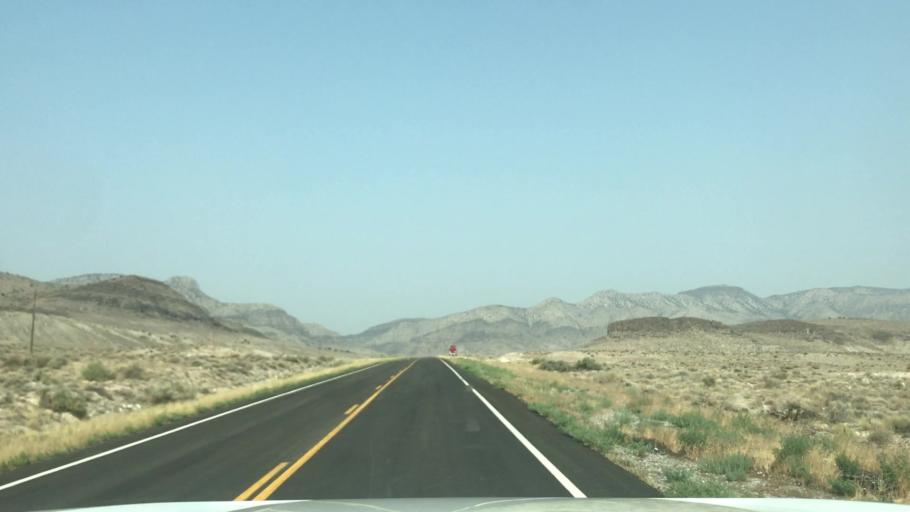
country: US
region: Utah
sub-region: Beaver County
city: Milford
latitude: 39.0843
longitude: -113.5066
